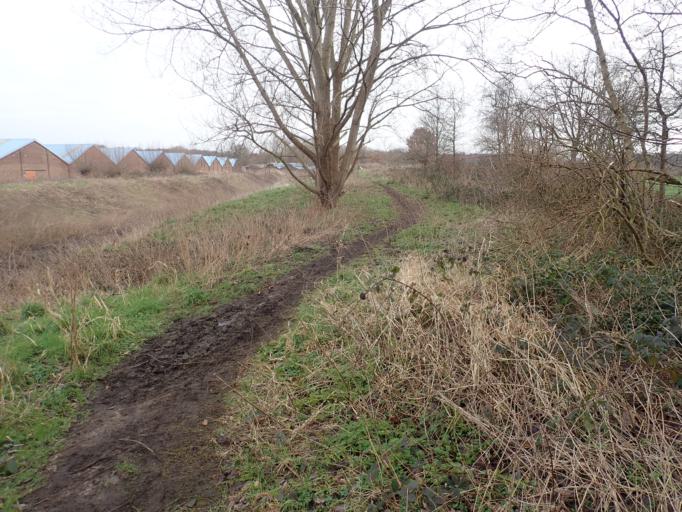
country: BE
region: Flanders
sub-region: Provincie Antwerpen
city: Schelle
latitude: 51.1313
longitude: 4.3423
